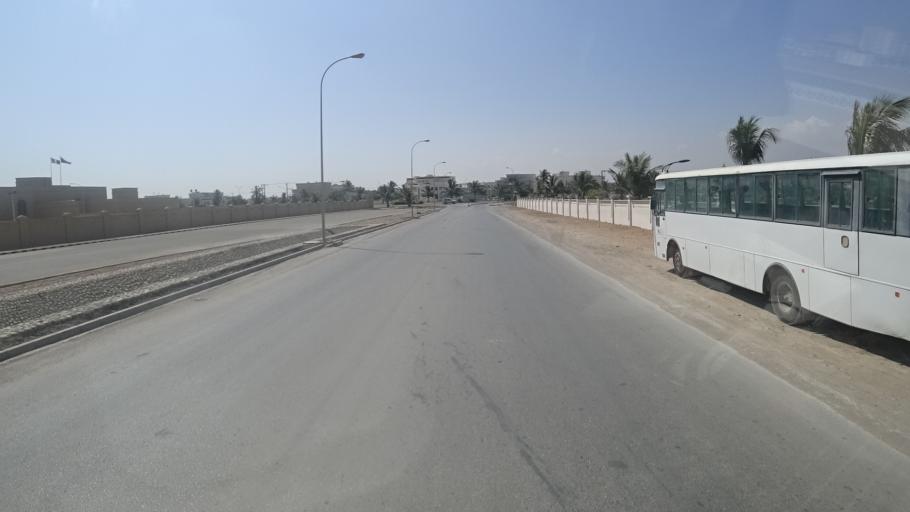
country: OM
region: Zufar
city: Salalah
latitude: 17.0167
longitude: 54.0373
